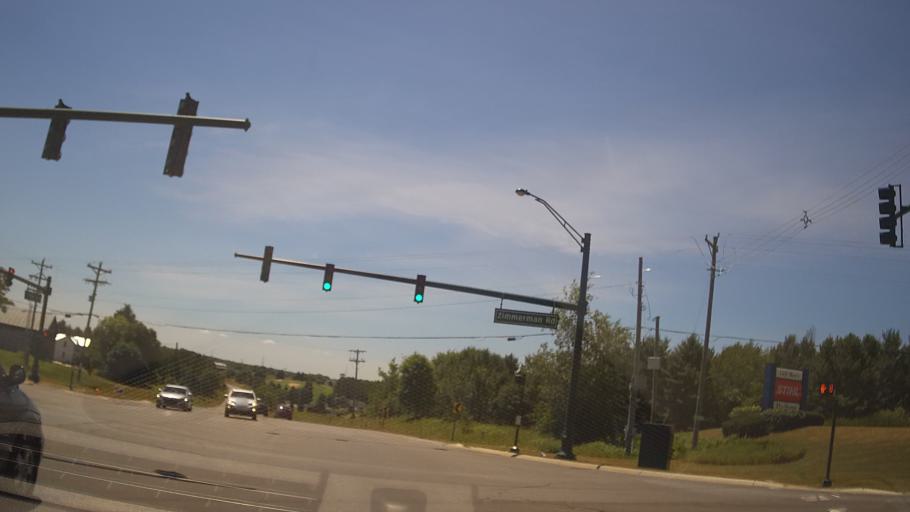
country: US
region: Michigan
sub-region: Grand Traverse County
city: Traverse City
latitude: 44.7259
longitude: -85.6763
